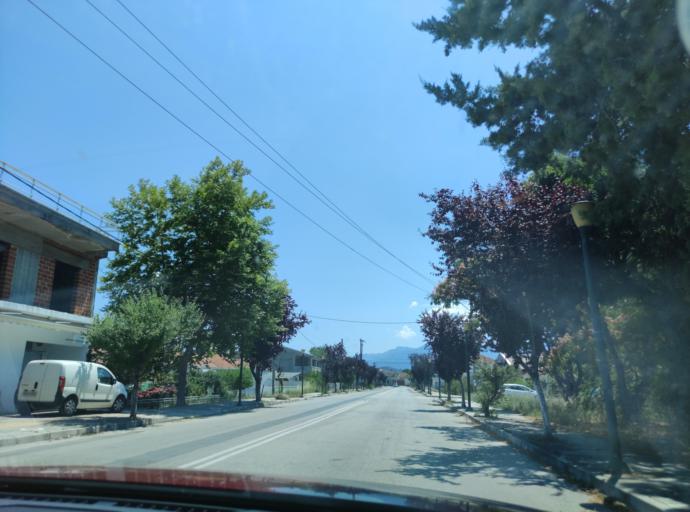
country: GR
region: East Macedonia and Thrace
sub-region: Nomos Kavalas
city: Keramoti
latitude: 40.8620
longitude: 24.7057
